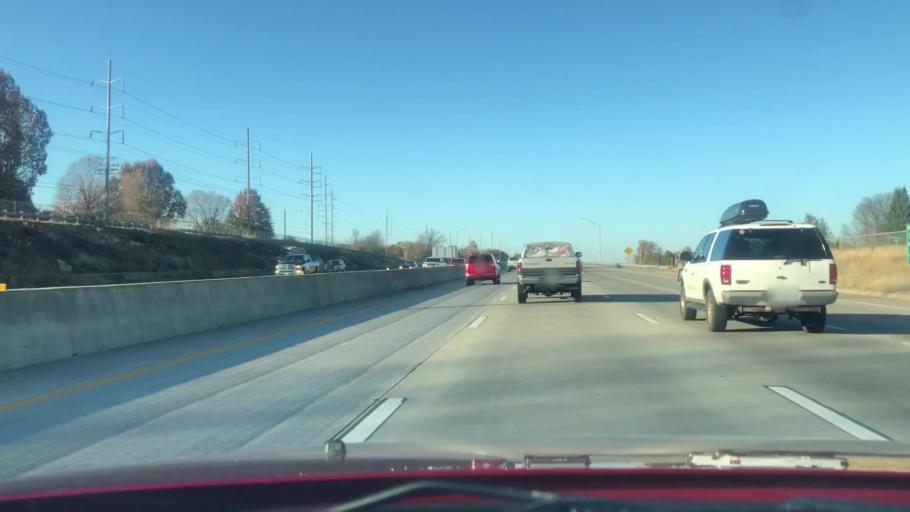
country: US
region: Missouri
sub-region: Greene County
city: Springfield
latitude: 37.1880
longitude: -93.2245
